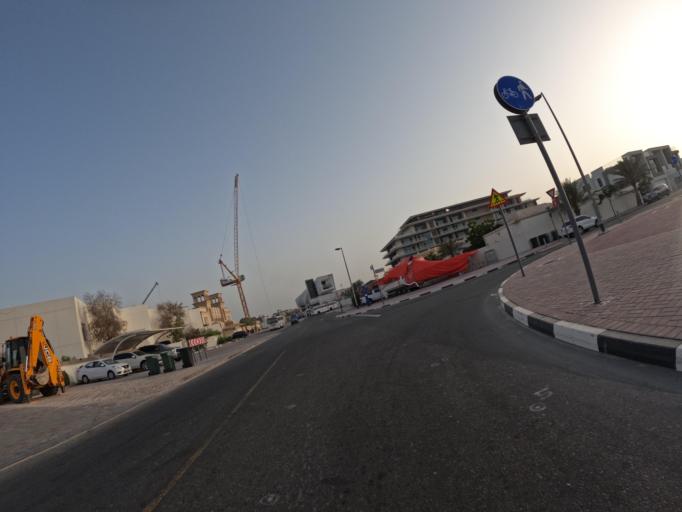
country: AE
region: Dubai
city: Dubai
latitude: 25.1949
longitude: 55.2424
